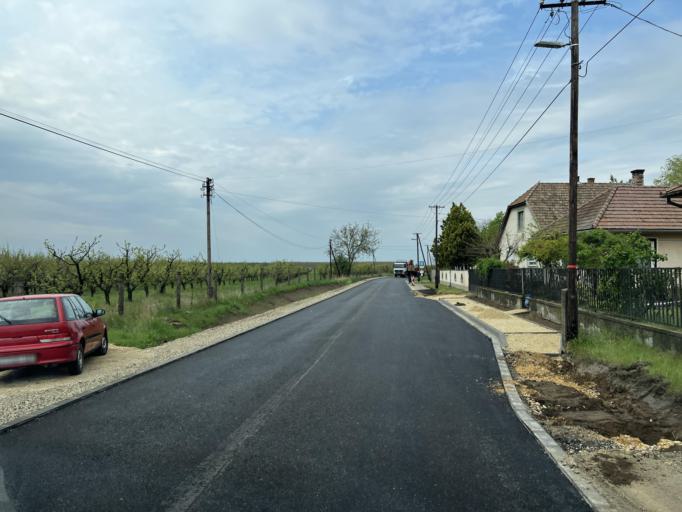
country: HU
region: Pest
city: Danszentmiklos
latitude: 47.1989
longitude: 19.5602
